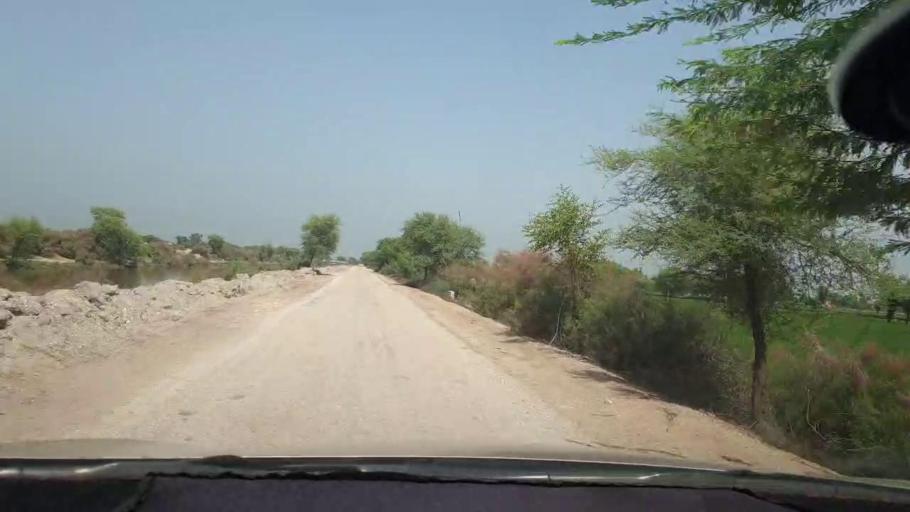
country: PK
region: Sindh
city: Kambar
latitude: 27.6668
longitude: 67.8927
